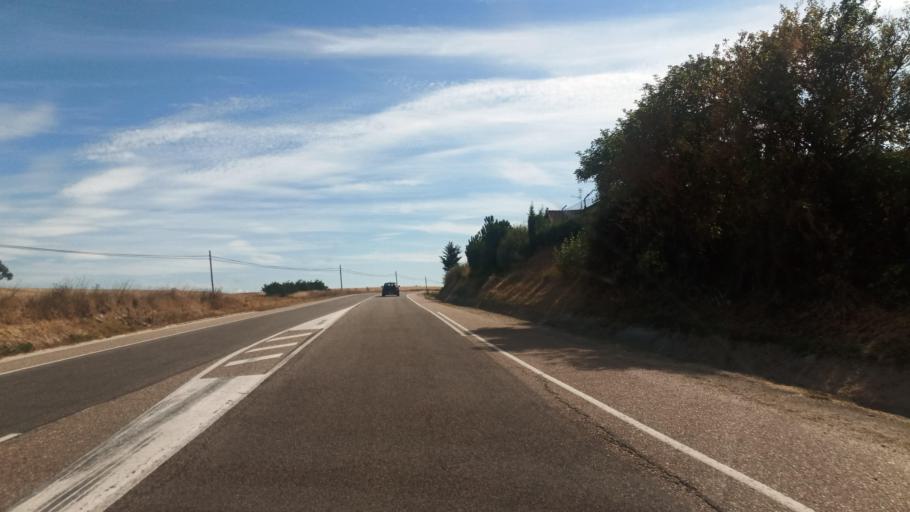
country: ES
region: Castille and Leon
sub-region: Provincia de Burgos
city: Briviesca
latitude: 42.5661
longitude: -3.3314
